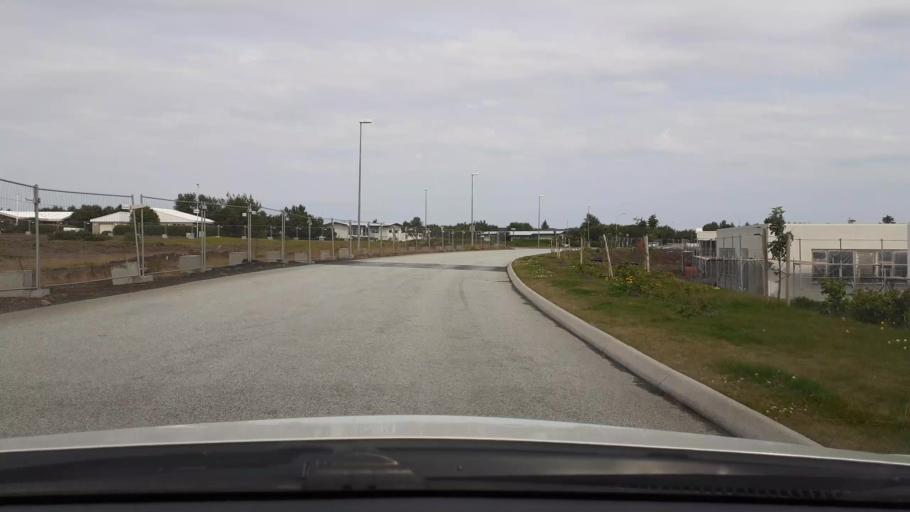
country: IS
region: Southern Peninsula
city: Reykjanesbaer
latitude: 63.9950
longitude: -22.5694
